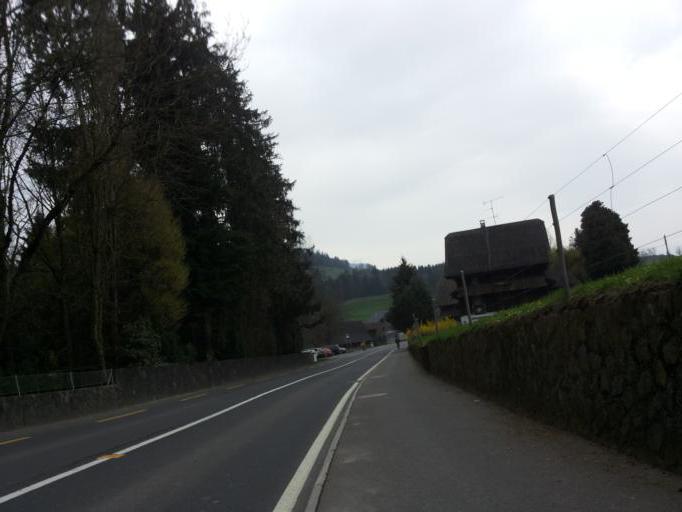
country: CH
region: Lucerne
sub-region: Lucerne-Land District
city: Meierskappel
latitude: 47.1187
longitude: 8.4630
